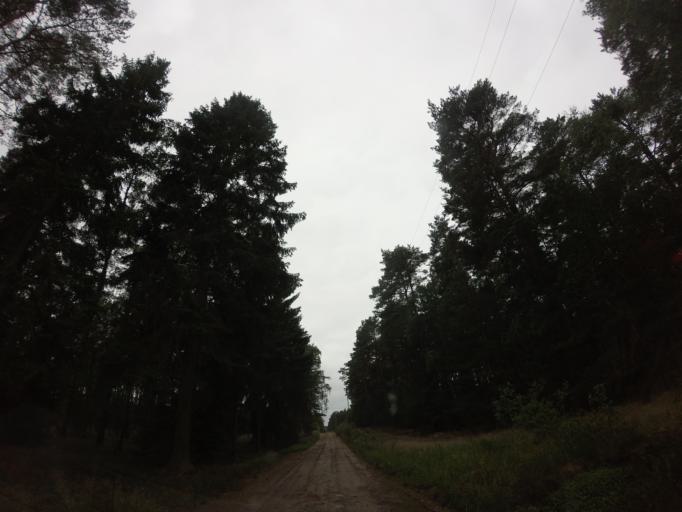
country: PL
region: West Pomeranian Voivodeship
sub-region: Powiat choszczenski
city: Drawno
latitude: 53.1408
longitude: 15.7292
